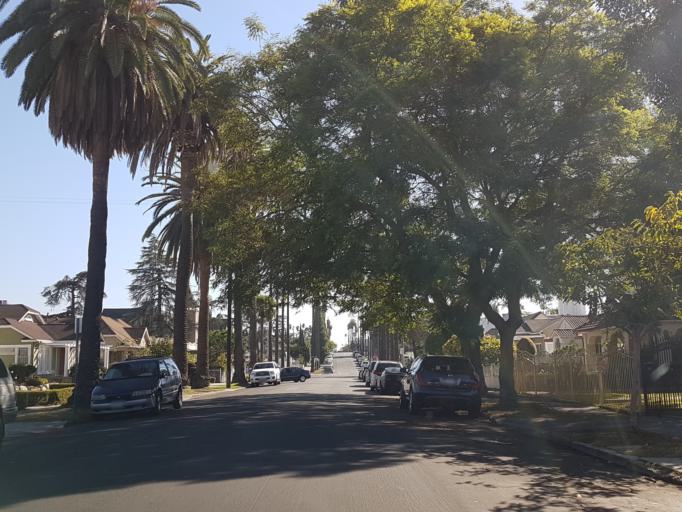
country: US
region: California
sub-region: Los Angeles County
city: Hollywood
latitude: 34.0506
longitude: -118.3101
